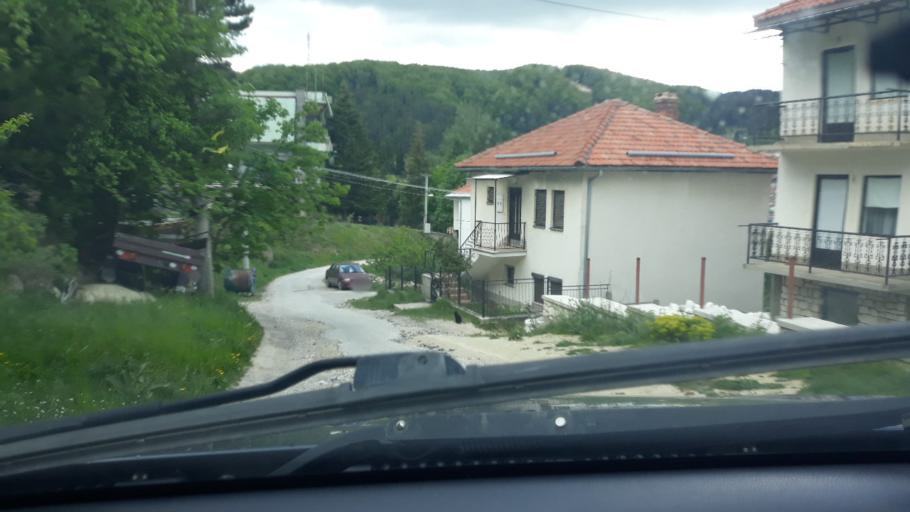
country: MK
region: Krusevo
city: Krushevo
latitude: 41.3651
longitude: 21.2543
